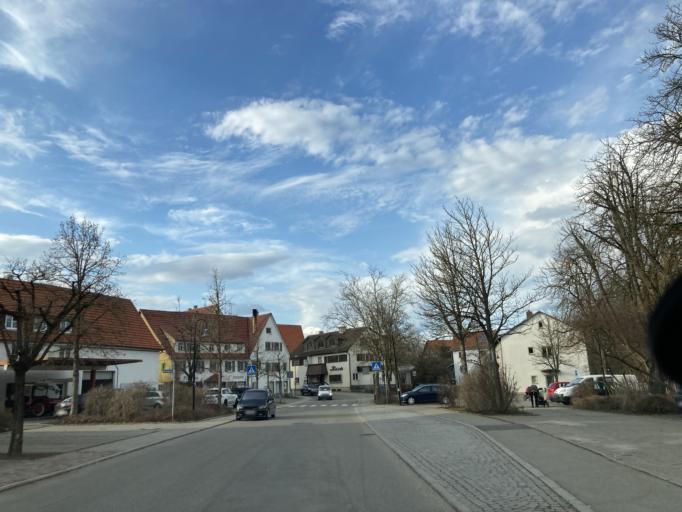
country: DE
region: Baden-Wuerttemberg
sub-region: Tuebingen Region
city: Dusslingen
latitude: 48.4515
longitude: 9.0550
